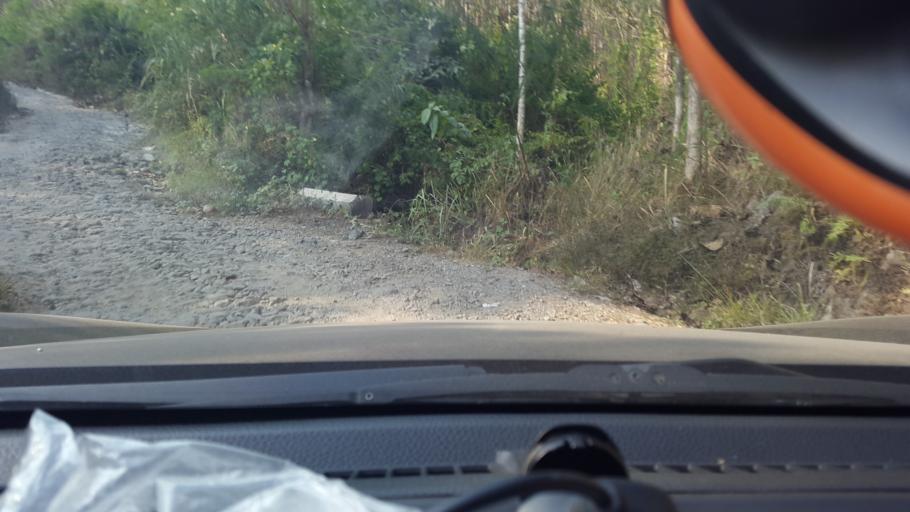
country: ID
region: West Java
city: Cikupa
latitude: -7.3574
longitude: 106.7040
